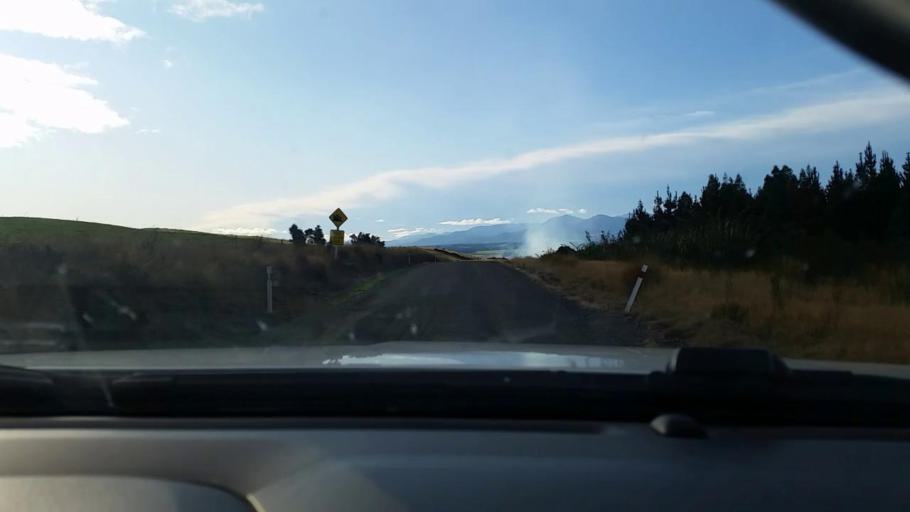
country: NZ
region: Southland
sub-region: Southland District
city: Winton
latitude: -45.8212
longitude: 168.1738
